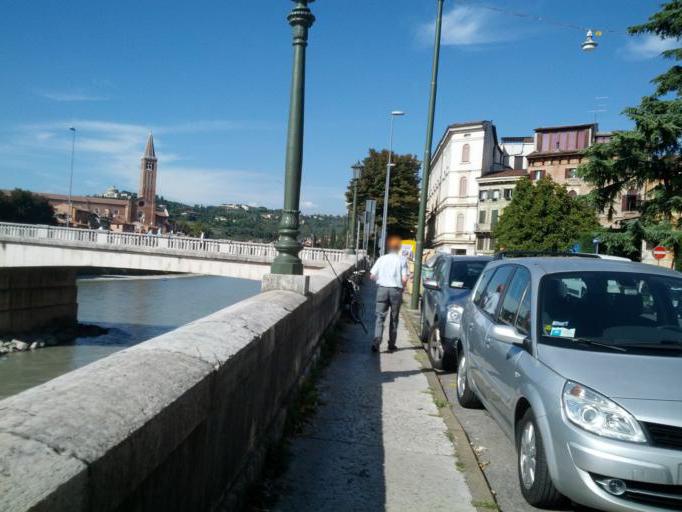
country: IT
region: Veneto
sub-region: Provincia di Verona
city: Verona
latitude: 45.4421
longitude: 11.0022
